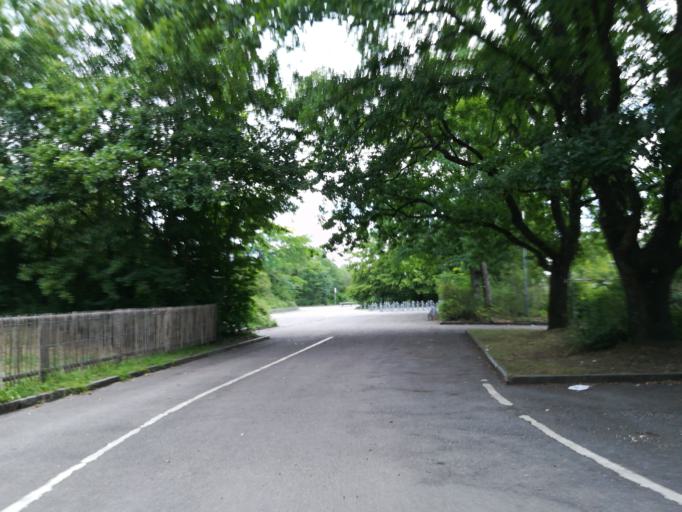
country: DE
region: Baden-Wuerttemberg
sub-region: Freiburg Region
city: Singen
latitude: 47.7531
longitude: 8.8360
